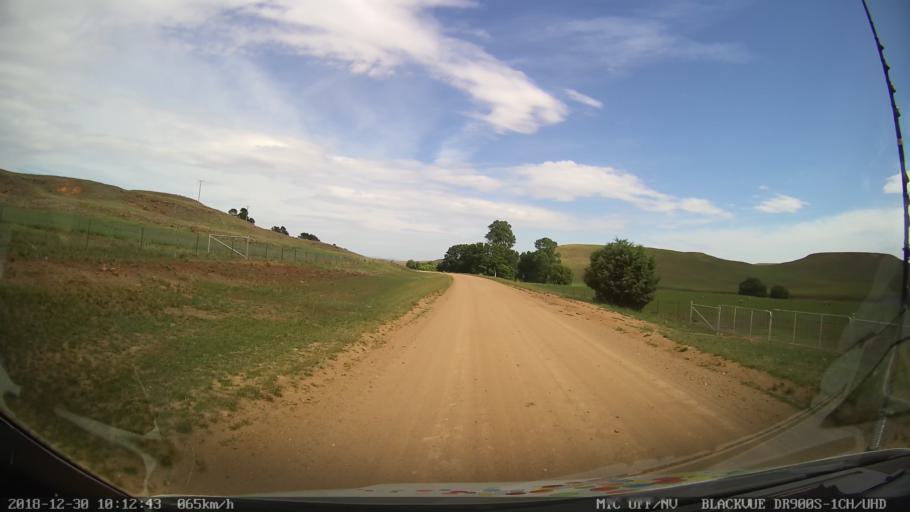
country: AU
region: New South Wales
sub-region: Snowy River
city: Berridale
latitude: -36.5399
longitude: 149.0731
